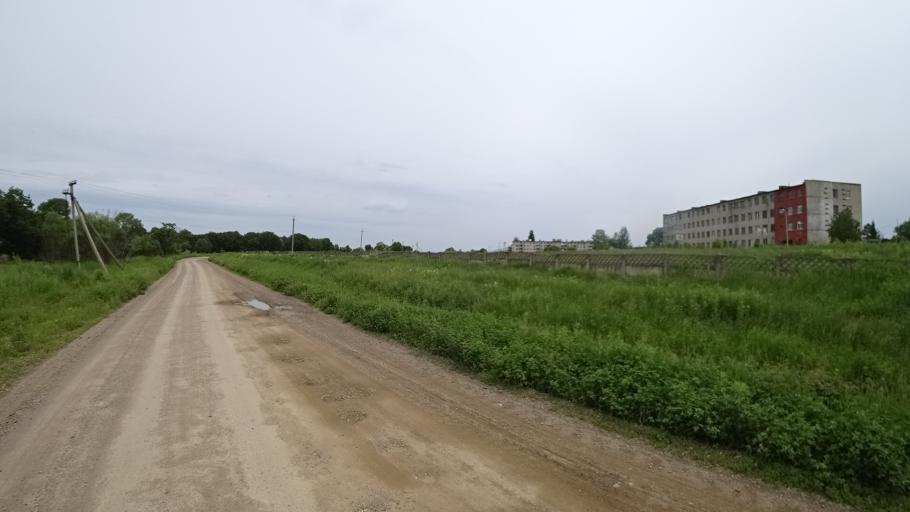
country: RU
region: Primorskiy
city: Arsen'yev
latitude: 44.2004
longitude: 133.3105
